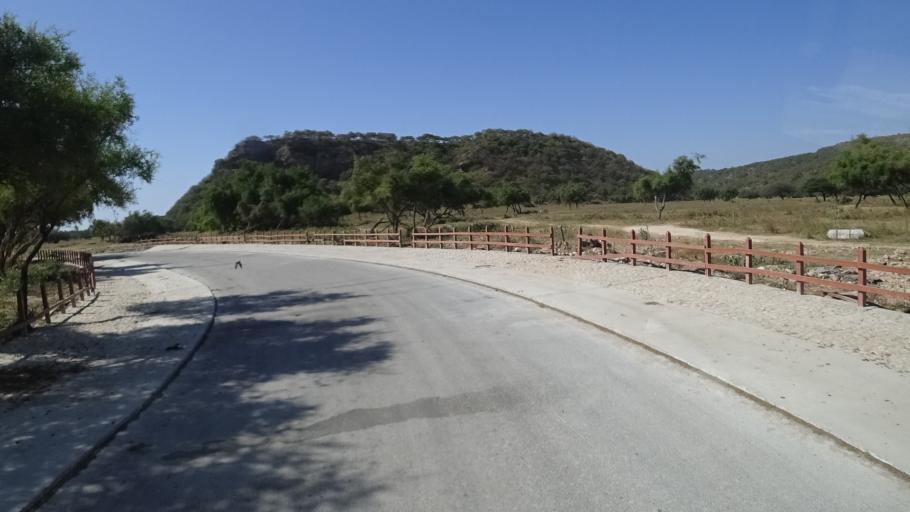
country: OM
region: Zufar
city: Salalah
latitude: 17.0893
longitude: 54.4335
